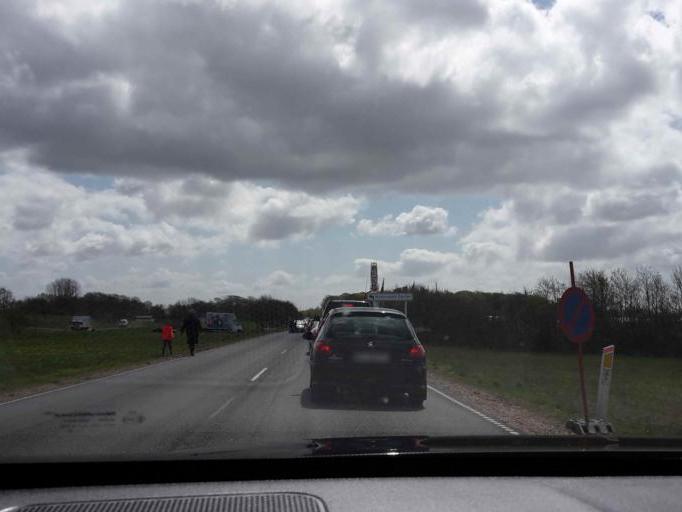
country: DK
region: South Denmark
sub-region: Esbjerg Kommune
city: Tjaereborg
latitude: 55.5290
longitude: 8.5835
